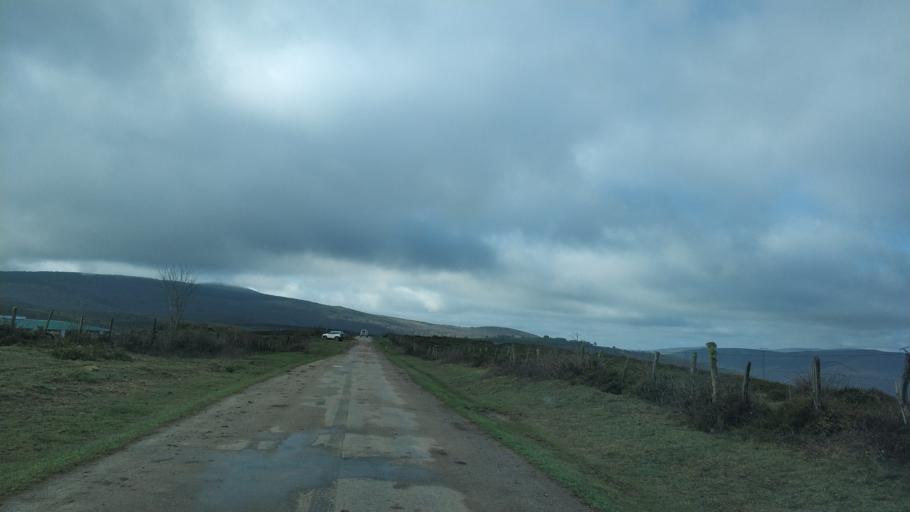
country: ES
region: Castille and Leon
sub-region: Provincia de Burgos
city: Arija
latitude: 42.9208
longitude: -3.9930
